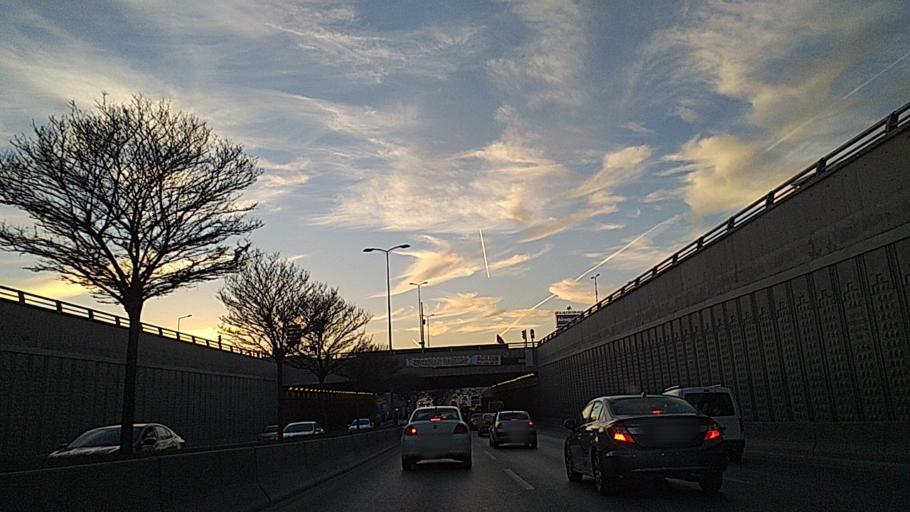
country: TR
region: Ankara
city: Etimesgut
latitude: 39.9654
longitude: 32.6374
